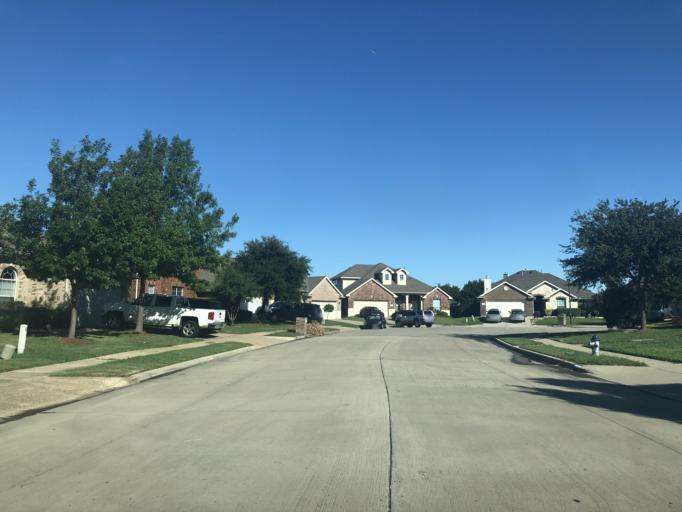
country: US
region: Texas
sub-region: Dallas County
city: Duncanville
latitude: 32.6582
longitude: -96.9686
